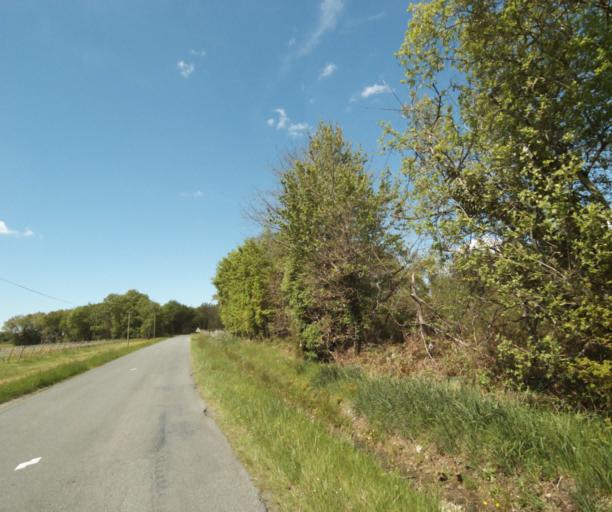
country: FR
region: Poitou-Charentes
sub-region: Departement de la Charente-Maritime
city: Burie
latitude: 45.7576
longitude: -0.4651
